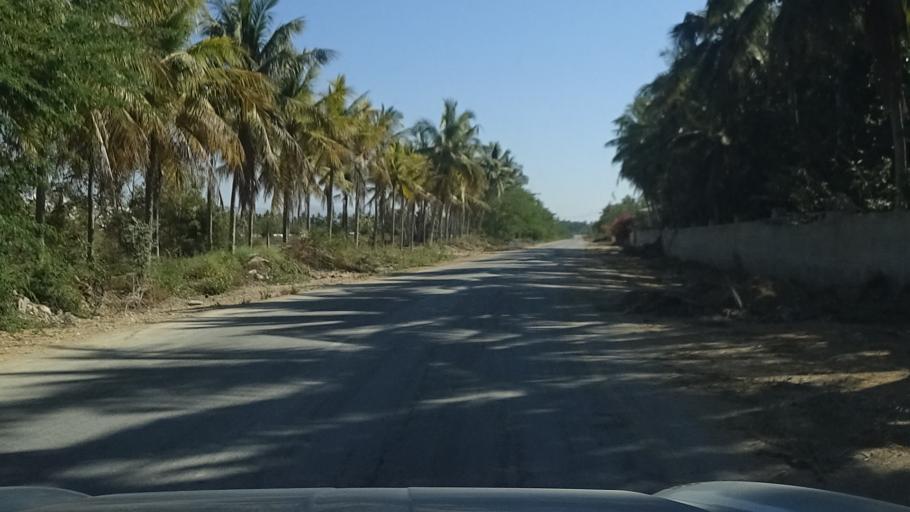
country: OM
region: Zufar
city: Salalah
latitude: 17.0322
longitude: 54.1456
